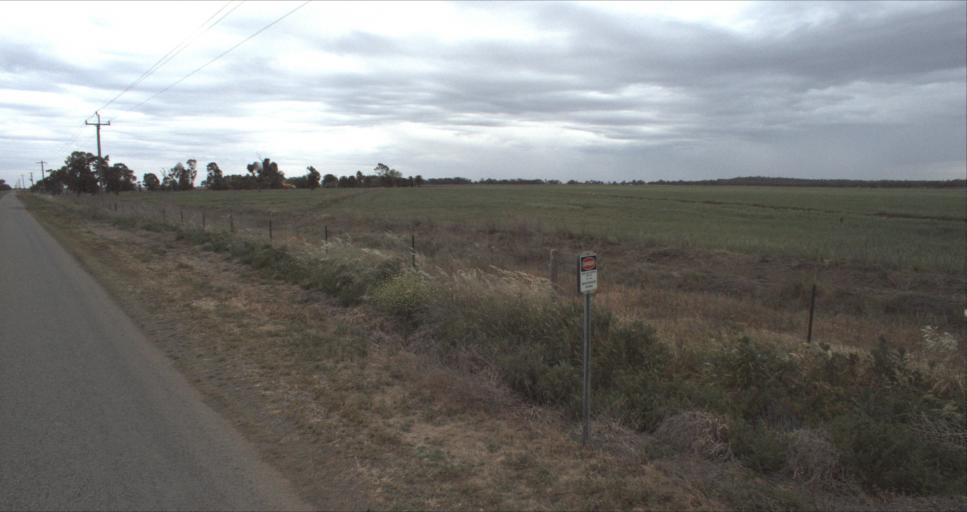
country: AU
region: New South Wales
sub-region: Leeton
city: Leeton
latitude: -34.4179
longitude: 146.3391
